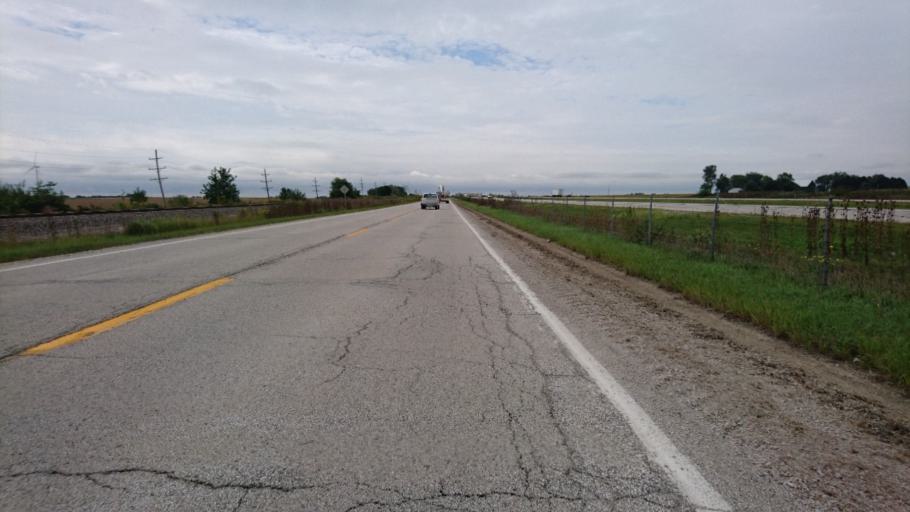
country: US
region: Illinois
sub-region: Livingston County
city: Odell
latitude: 41.0345
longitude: -88.4962
